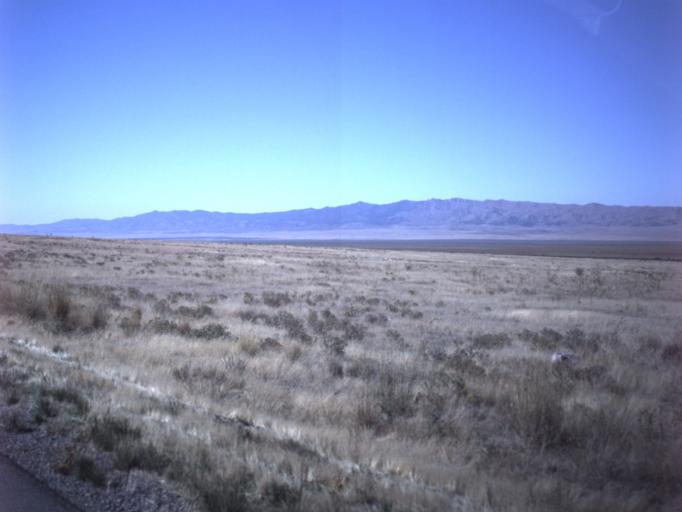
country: US
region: Utah
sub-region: Tooele County
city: Grantsville
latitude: 40.5986
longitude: -112.7149
